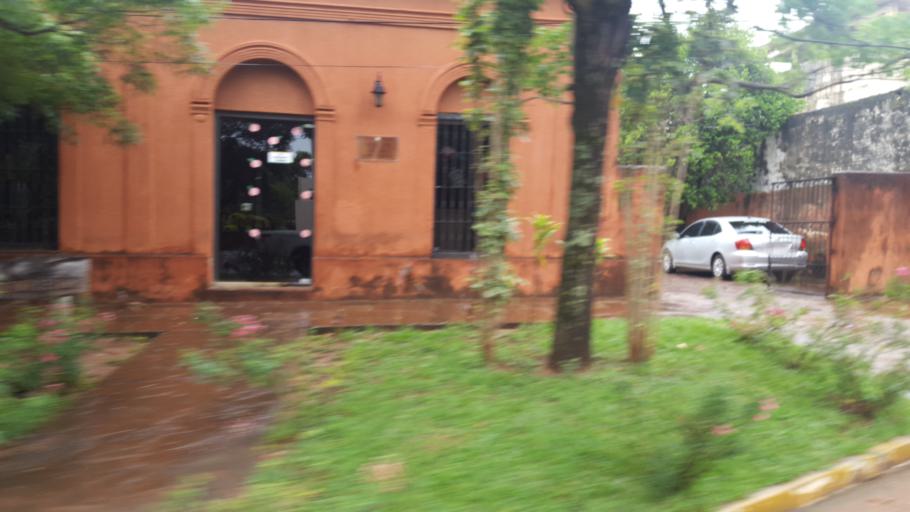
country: PY
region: Misiones
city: San Juan Bautista
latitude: -26.6689
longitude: -57.1465
